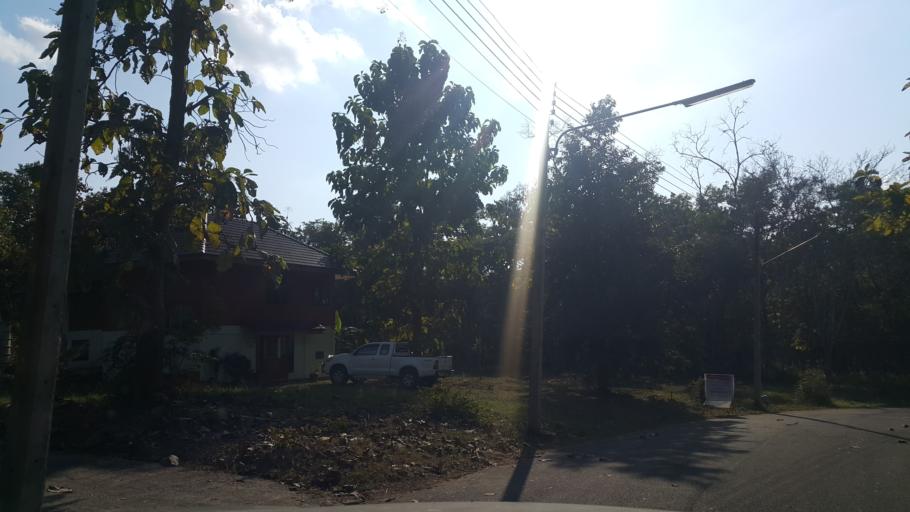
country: TH
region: Lamphun
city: Mae Tha
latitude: 18.5116
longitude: 99.1015
